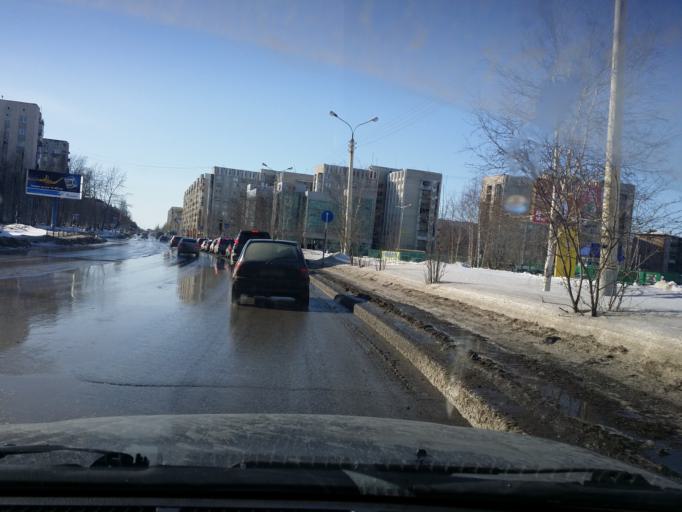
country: RU
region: Khanty-Mansiyskiy Avtonomnyy Okrug
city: Nizhnevartovsk
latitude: 60.9455
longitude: 76.5689
